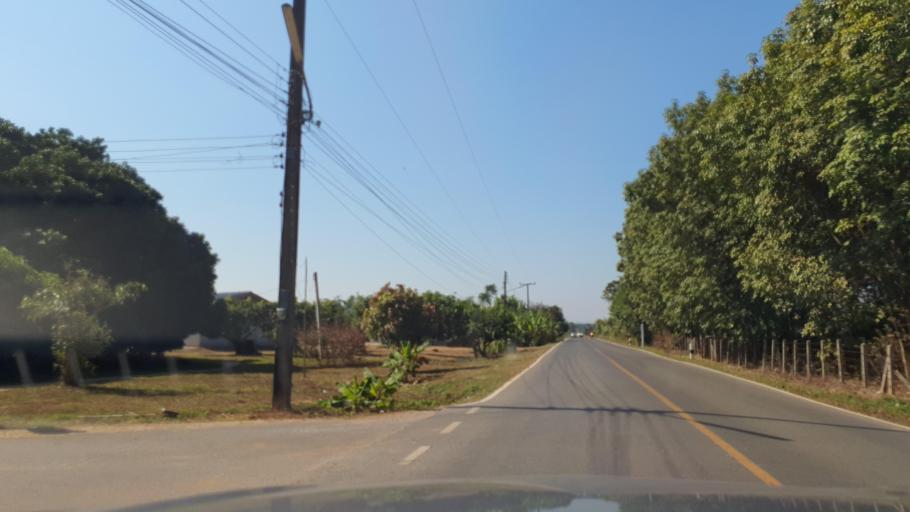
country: TH
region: Nan
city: Pua
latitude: 19.1323
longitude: 100.9291
